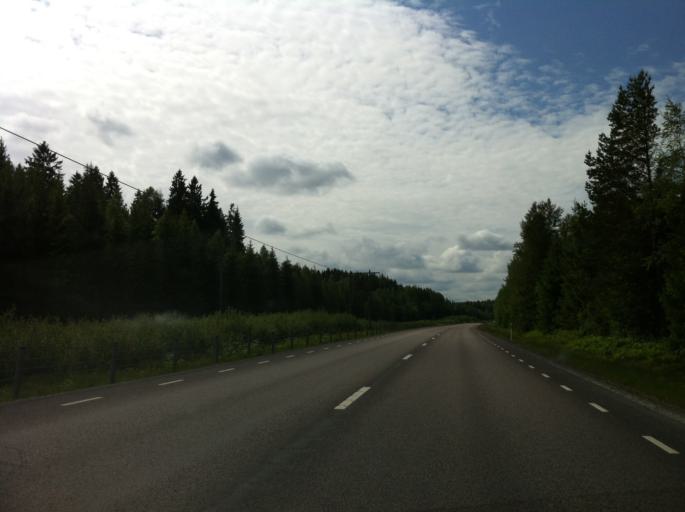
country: SE
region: Vaermland
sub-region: Karlstads Kommun
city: Edsvalla
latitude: 59.4337
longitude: 13.2004
